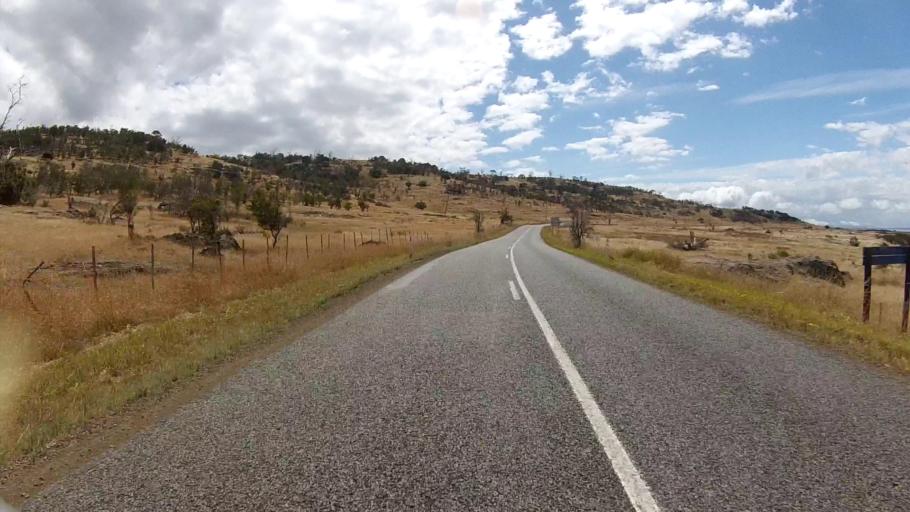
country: AU
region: Tasmania
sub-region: Sorell
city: Sorell
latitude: -42.1827
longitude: 148.0670
